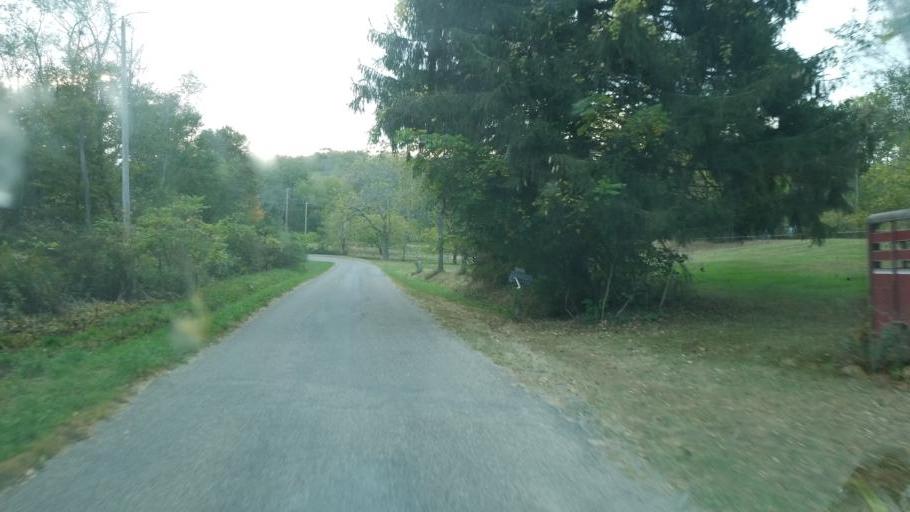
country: US
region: Ohio
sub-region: Ashland County
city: Loudonville
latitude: 40.7043
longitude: -82.2295
